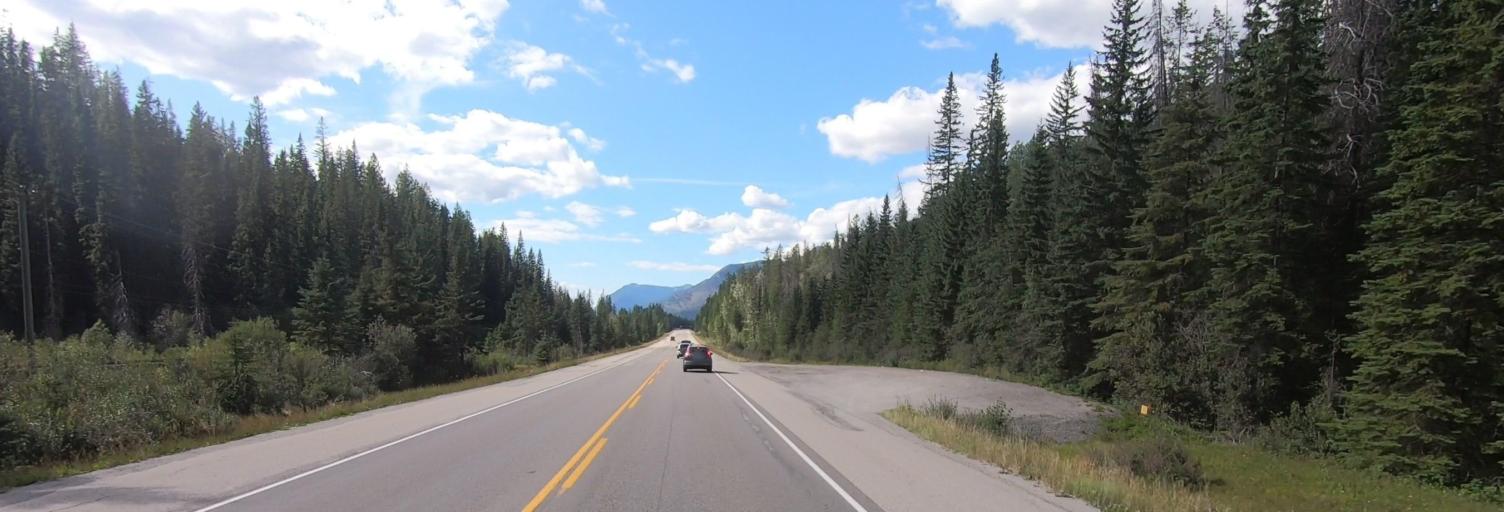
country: CA
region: British Columbia
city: Golden
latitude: 51.2263
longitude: -116.6278
